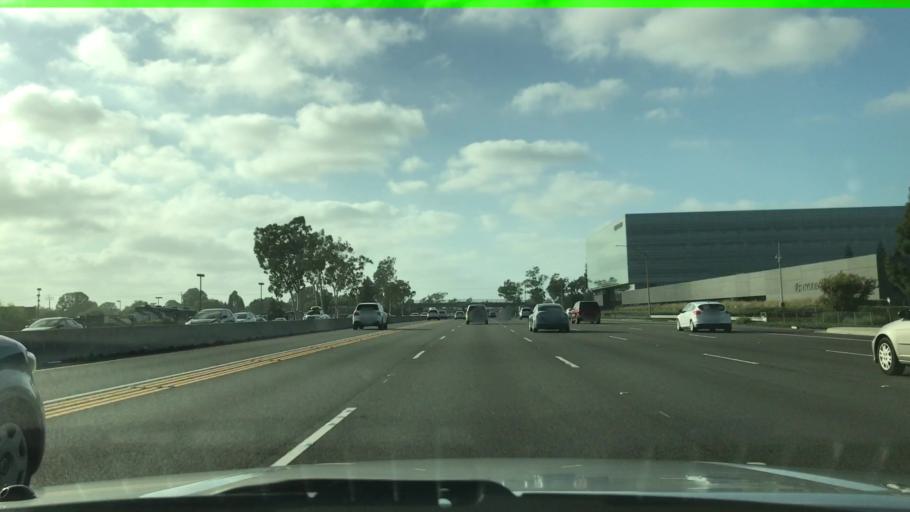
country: US
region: California
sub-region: Orange County
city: Fountain Valley
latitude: 33.6981
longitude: -117.9408
